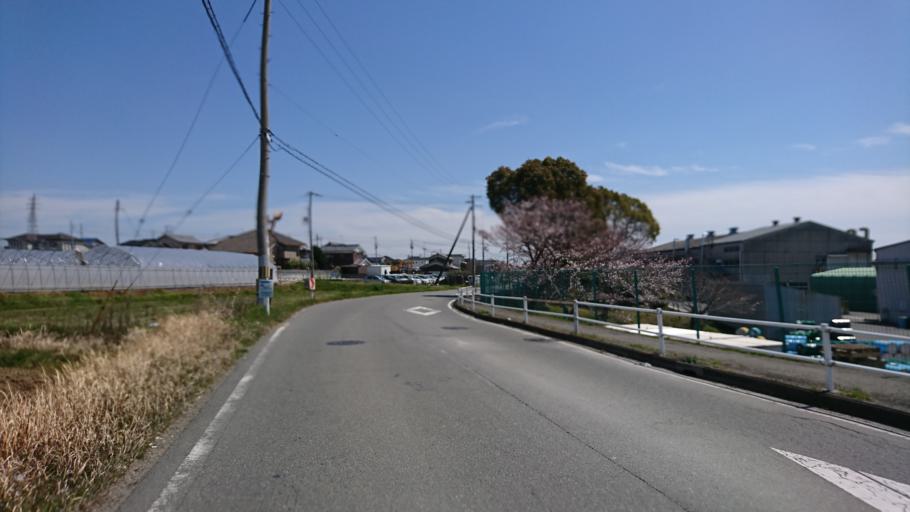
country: JP
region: Hyogo
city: Kakogawacho-honmachi
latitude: 34.7312
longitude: 134.9013
